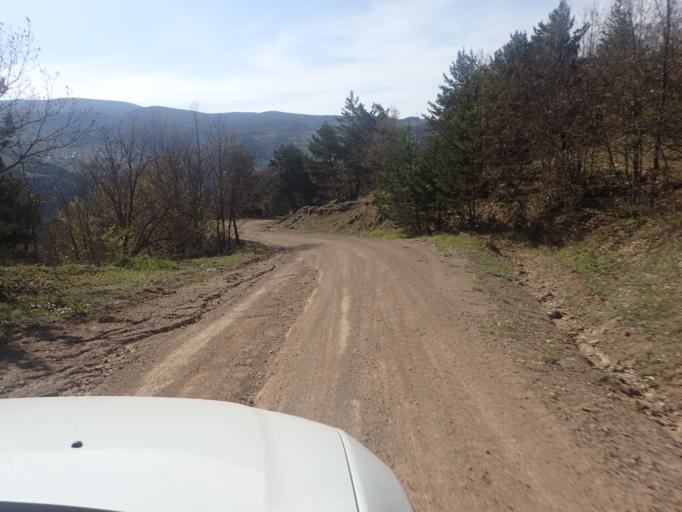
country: TR
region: Ordu
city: Mesudiye
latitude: 40.4289
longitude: 37.8157
